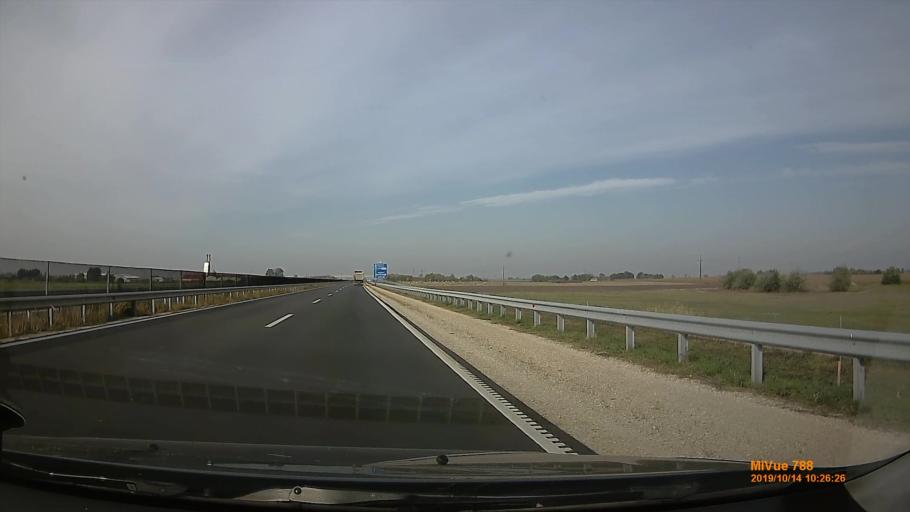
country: HU
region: Pest
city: Cegled
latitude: 47.1933
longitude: 19.8374
